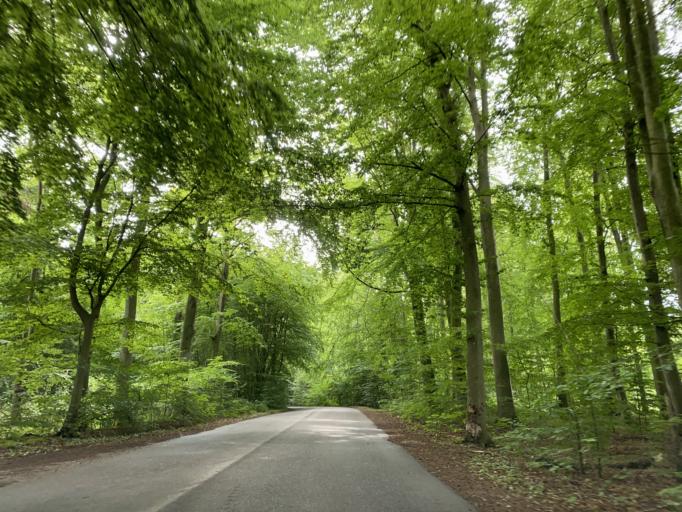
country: DK
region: South Denmark
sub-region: Sonderborg Kommune
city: Sonderborg
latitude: 54.9097
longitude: 9.8315
